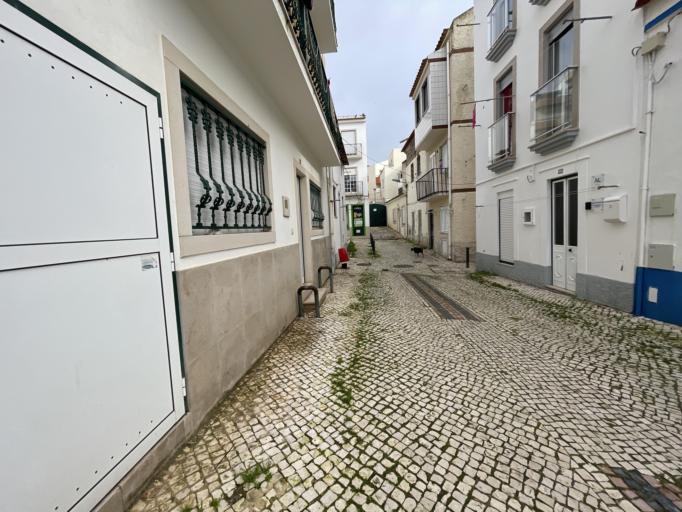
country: PT
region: Leiria
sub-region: Nazare
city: Nazare
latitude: 39.6028
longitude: -9.0733
